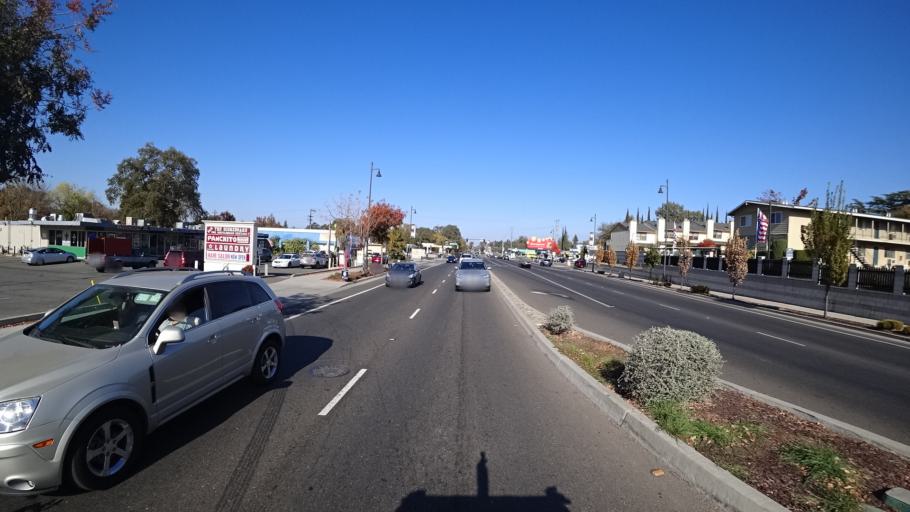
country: US
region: California
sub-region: Sacramento County
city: Citrus Heights
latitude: 38.7053
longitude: -121.2905
